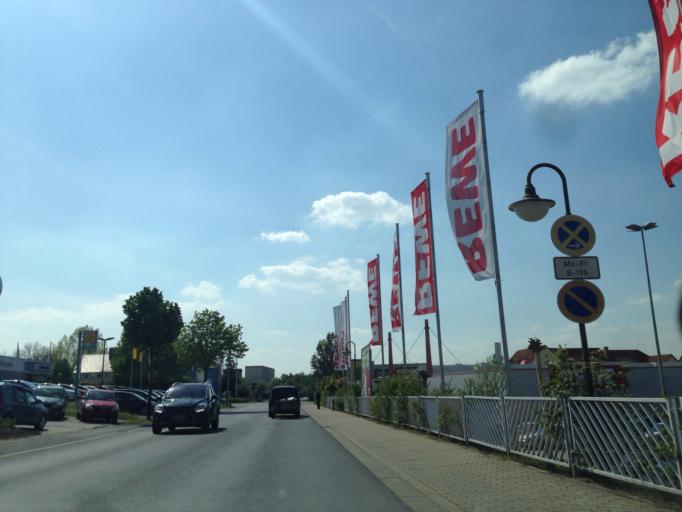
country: DE
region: Thuringia
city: Bodelwitz
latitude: 50.6980
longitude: 11.6187
